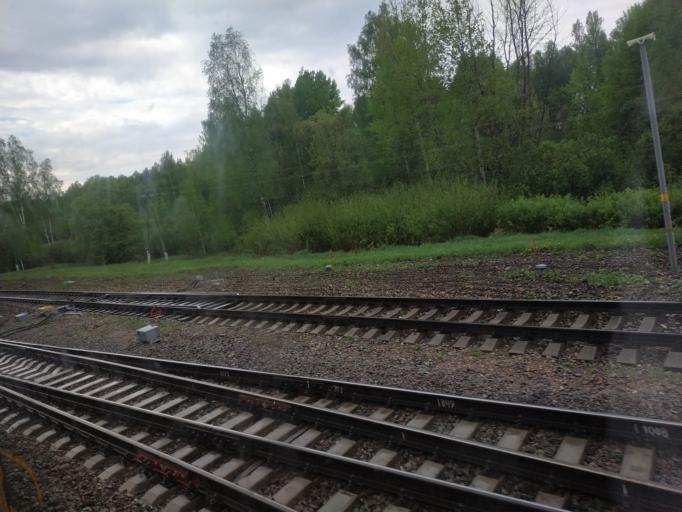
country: RU
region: Kaluga
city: Baryatino
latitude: 54.3523
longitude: 34.3267
